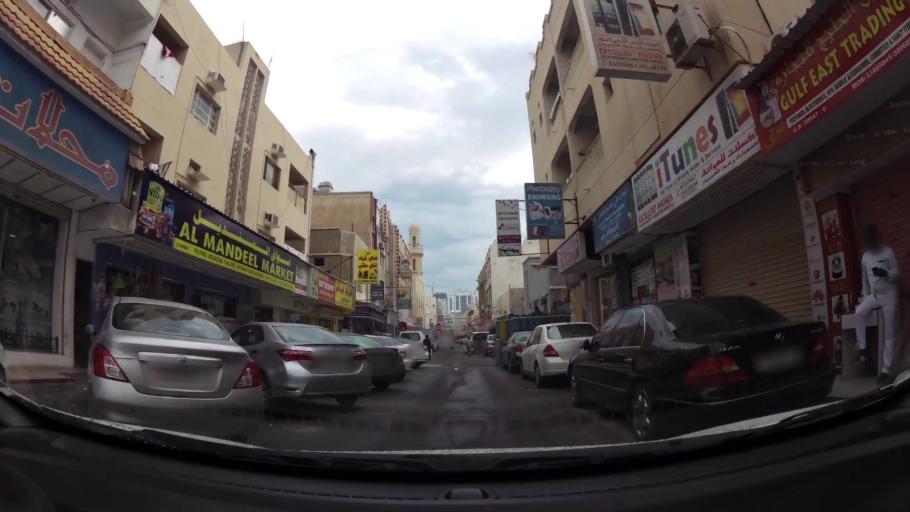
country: BH
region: Manama
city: Manama
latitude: 26.2280
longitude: 50.5902
